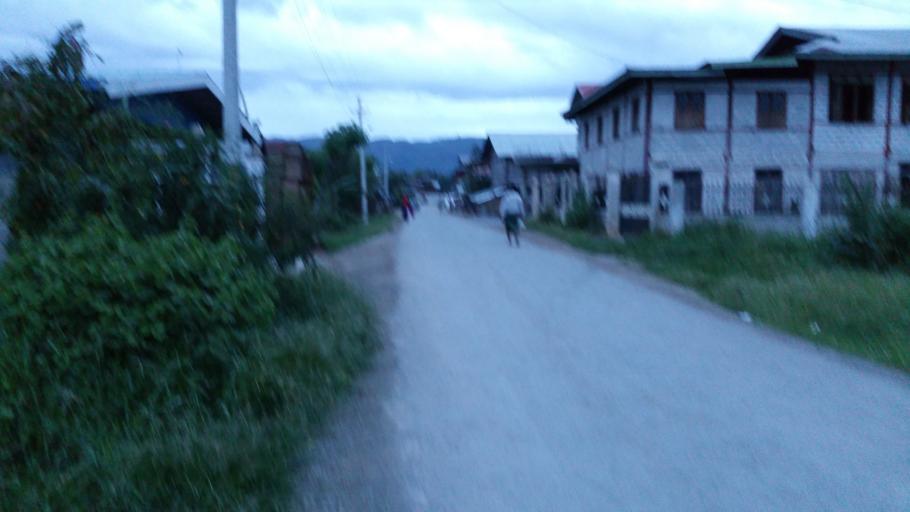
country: MM
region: Shan
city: Taunggyi
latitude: 20.6567
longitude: 96.9262
